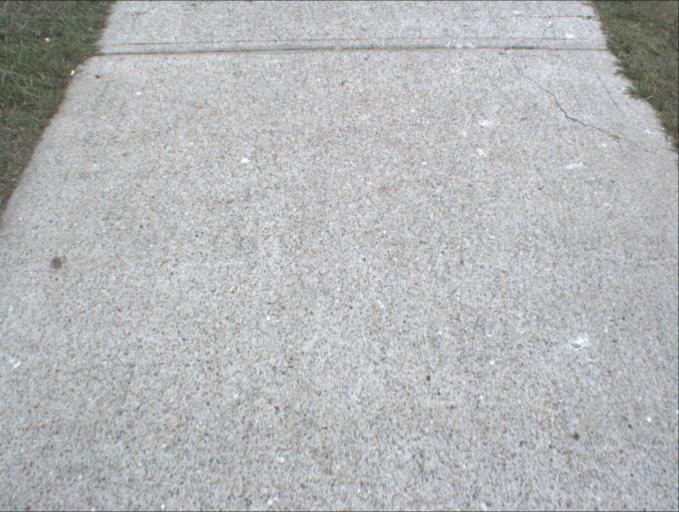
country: AU
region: Queensland
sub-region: Logan
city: Beenleigh
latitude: -27.7088
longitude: 153.2003
